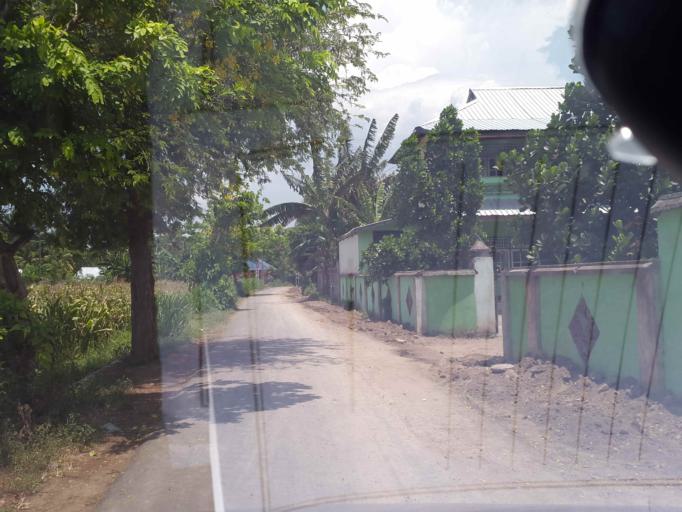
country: ID
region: West Nusa Tenggara
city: Jelateng Timur
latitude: -8.7065
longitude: 116.0796
